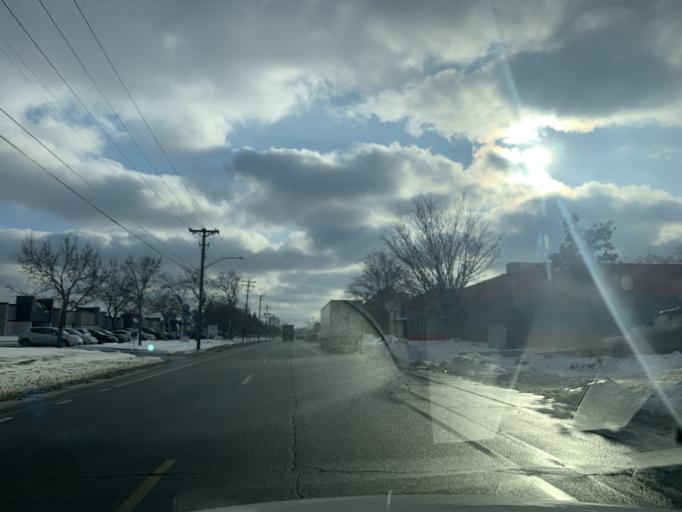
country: US
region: Minnesota
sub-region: Anoka County
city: Columbia Heights
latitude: 45.0107
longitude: -93.2805
